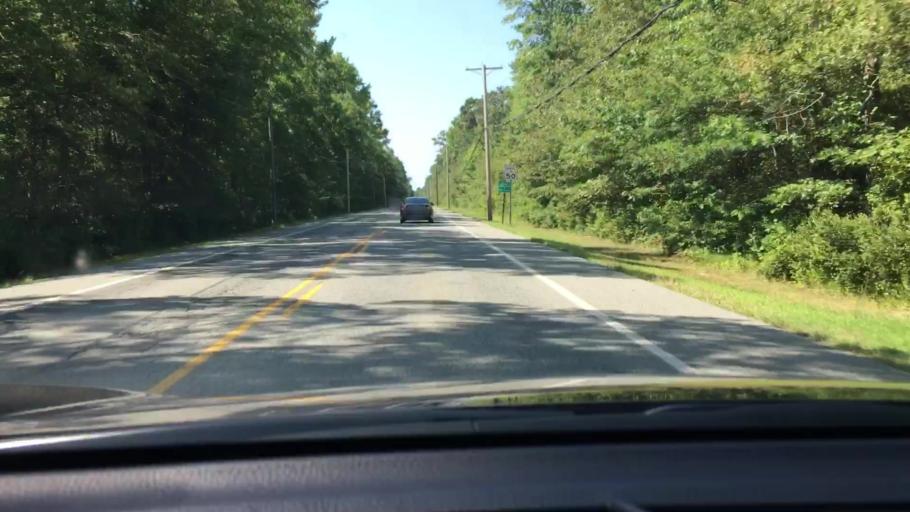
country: US
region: New Jersey
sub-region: Cape May County
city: Woodbine
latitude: 39.2939
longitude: -74.7828
